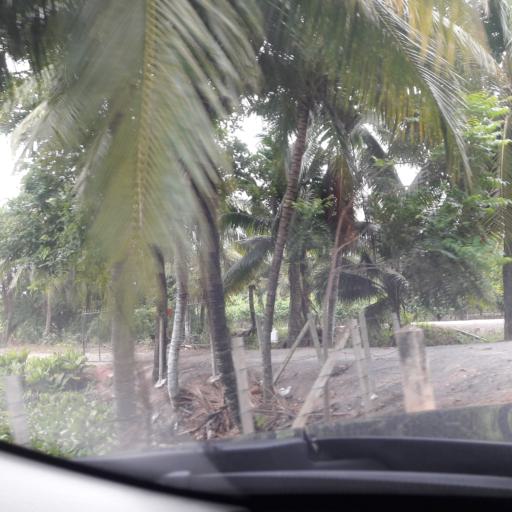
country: TH
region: Ratchaburi
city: Damnoen Saduak
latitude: 13.5746
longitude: 99.9451
